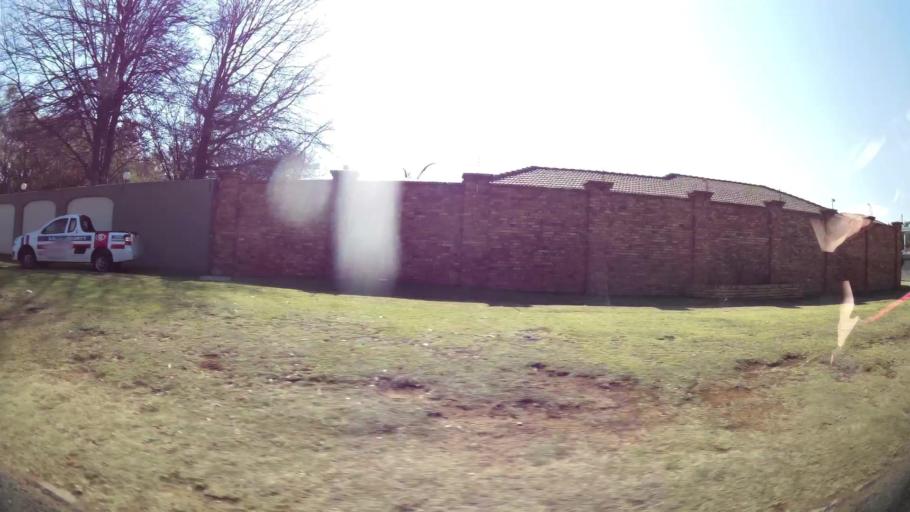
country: ZA
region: Gauteng
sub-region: Ekurhuleni Metropolitan Municipality
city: Boksburg
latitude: -26.1679
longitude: 28.2609
